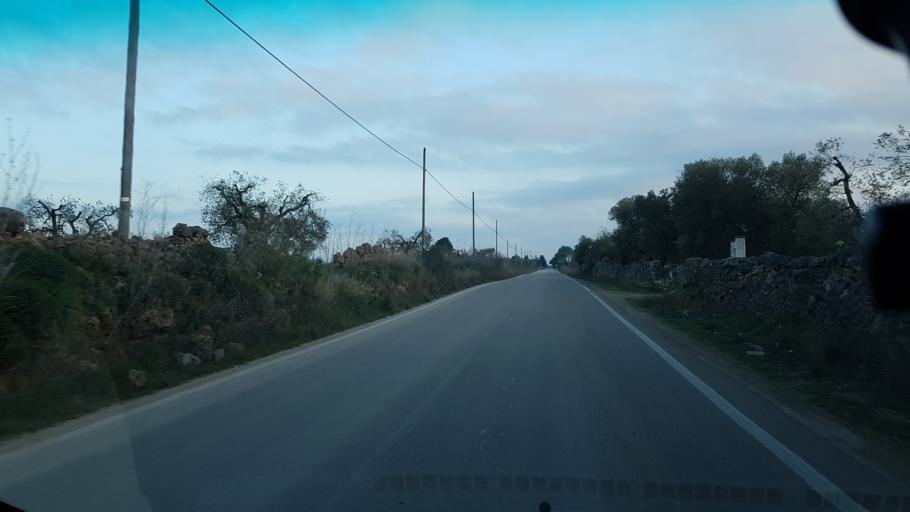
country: IT
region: Apulia
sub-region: Provincia di Brindisi
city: San Vito dei Normanni
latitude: 40.6480
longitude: 17.7756
